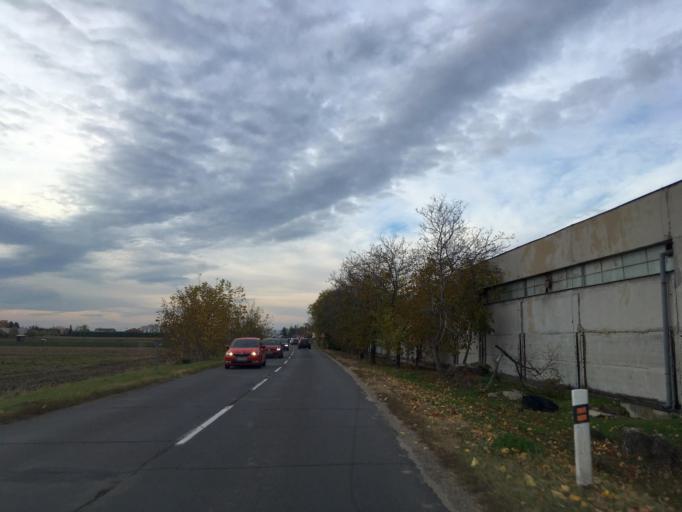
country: SK
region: Trnavsky
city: Dunajska Streda
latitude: 48.0135
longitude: 17.5791
